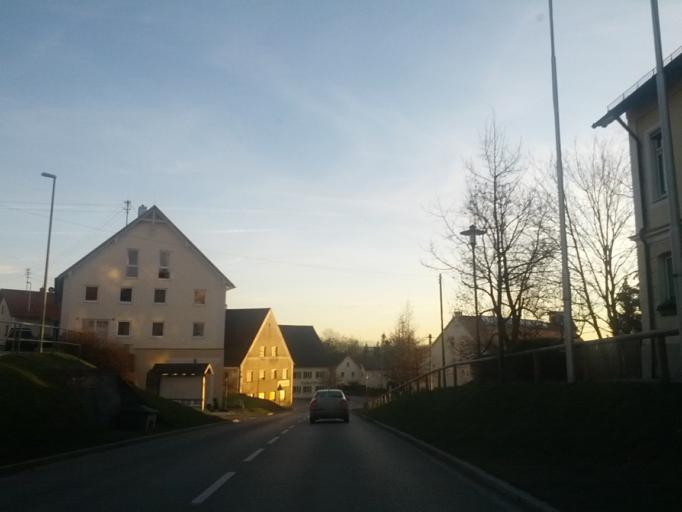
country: DE
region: Bavaria
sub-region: Swabia
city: Heimertingen
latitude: 48.0413
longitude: 10.1537
